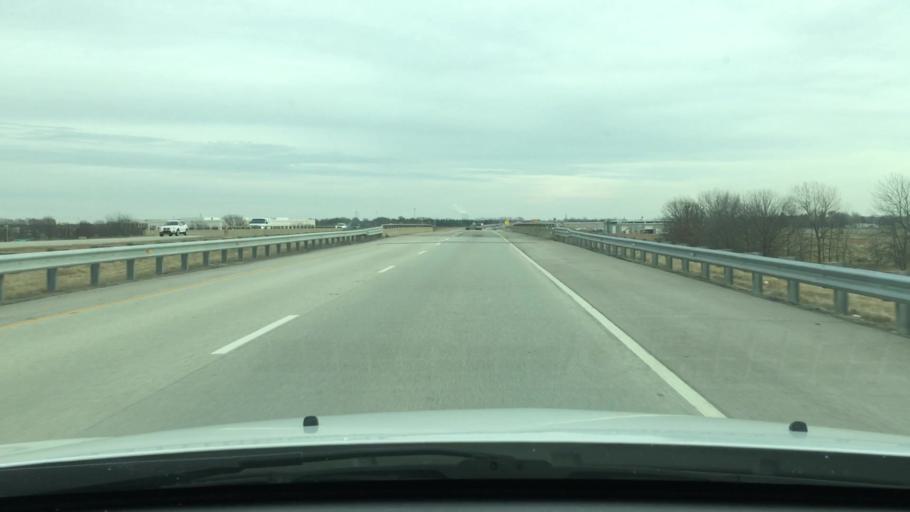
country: US
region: Illinois
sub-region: Sangamon County
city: Jerome
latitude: 39.7518
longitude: -89.7519
